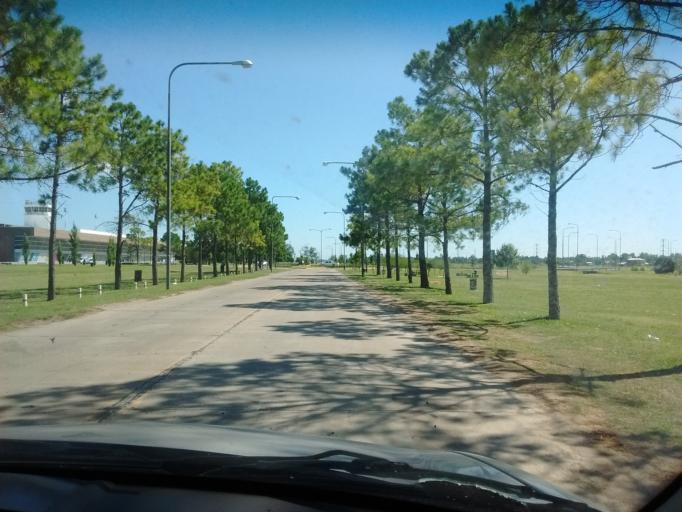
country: AR
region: Santa Fe
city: Funes
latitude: -32.9194
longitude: -60.7803
